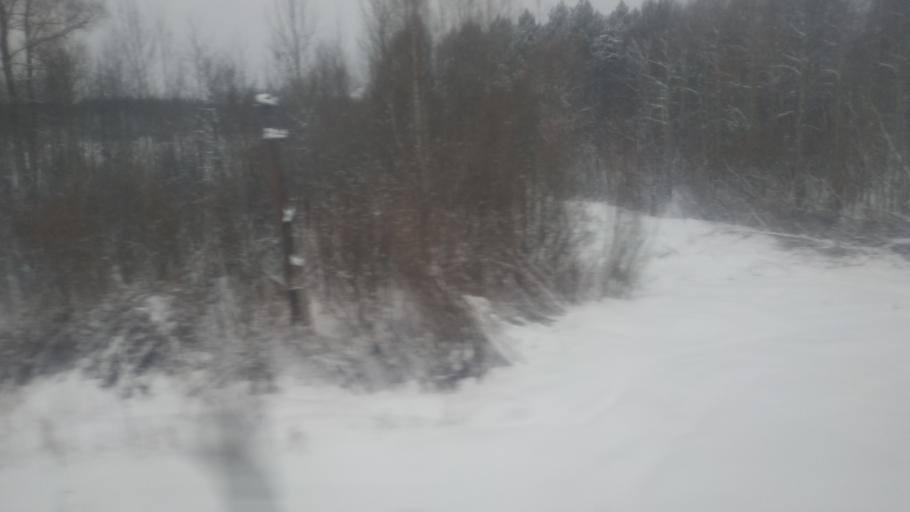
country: RU
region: Bashkortostan
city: Yanaul
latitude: 56.2520
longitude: 54.6970
